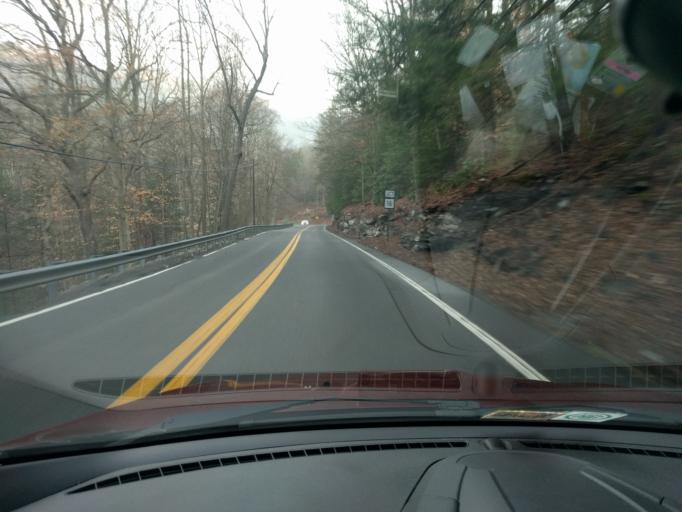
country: US
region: West Virginia
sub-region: Fayette County
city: Ansted
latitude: 38.1363
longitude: -81.1467
